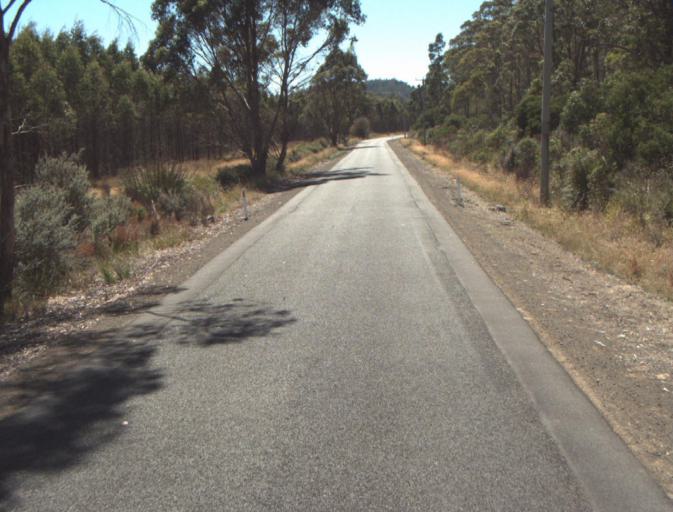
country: AU
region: Tasmania
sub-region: Launceston
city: Newstead
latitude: -41.3277
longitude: 147.3125
